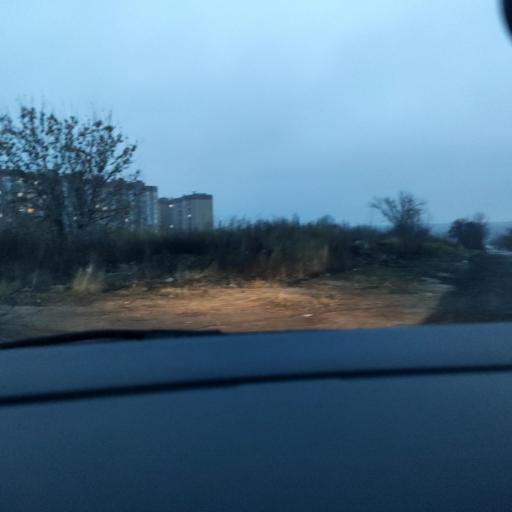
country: RU
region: Voronezj
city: Shilovo
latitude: 51.5737
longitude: 39.1329
